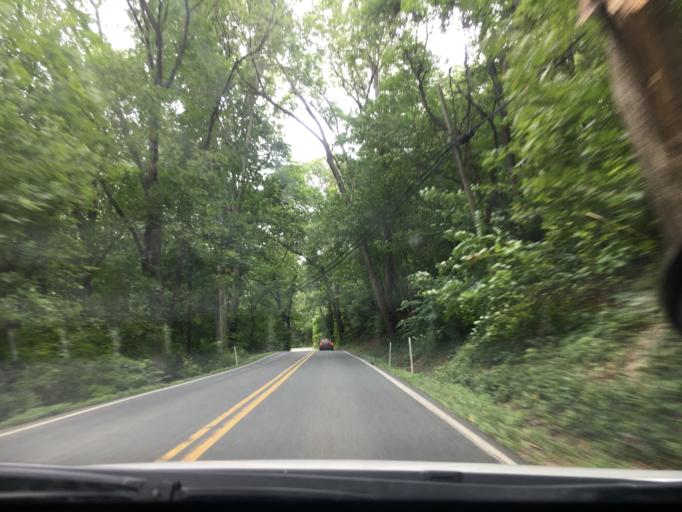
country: US
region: Virginia
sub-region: City of Charlottesville
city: Charlottesville
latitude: 37.9983
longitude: -78.4517
